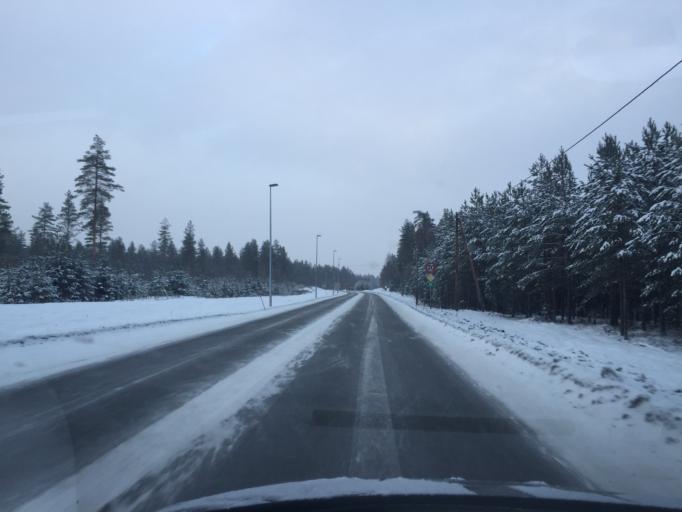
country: NO
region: Hedmark
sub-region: Elverum
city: Elverum
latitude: 60.9025
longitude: 11.5992
